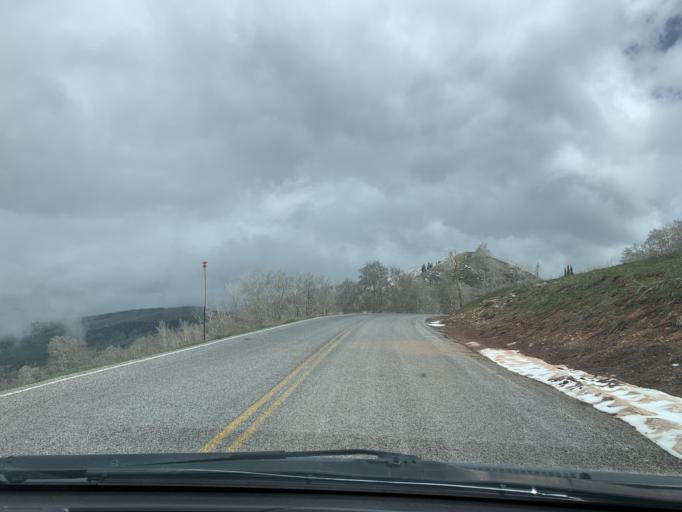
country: US
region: Utah
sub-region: Utah County
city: Santaquin
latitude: 39.8614
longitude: -111.6941
